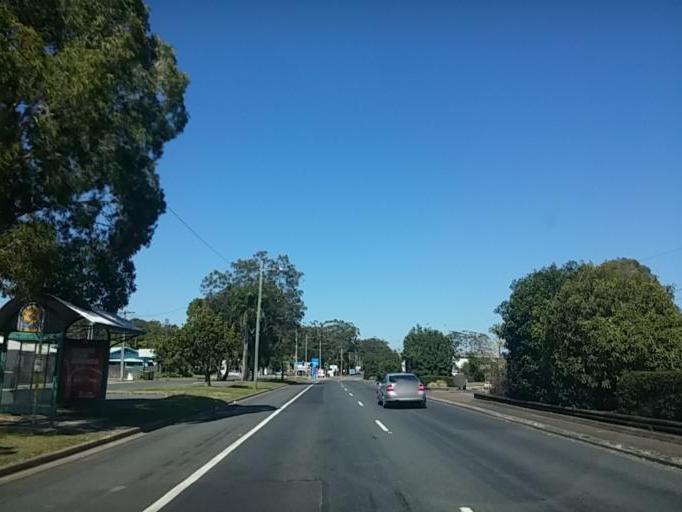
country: AU
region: New South Wales
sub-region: Coffs Harbour
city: Coffs Harbour
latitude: -30.2888
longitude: 153.1227
